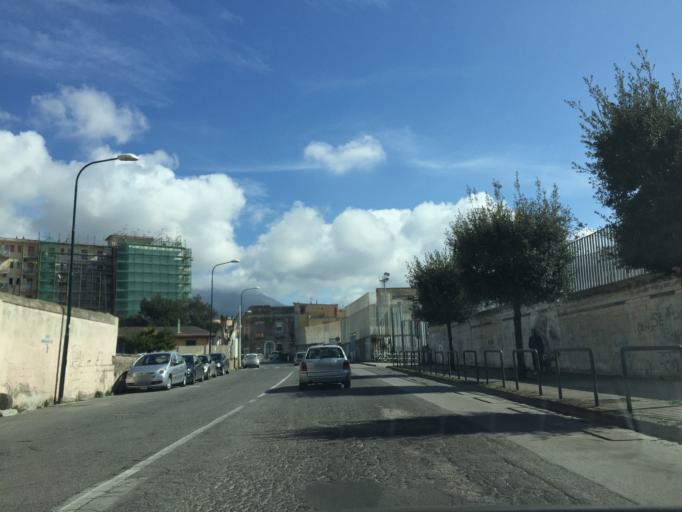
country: IT
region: Campania
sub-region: Provincia di Napoli
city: Portici
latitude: 40.8246
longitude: 14.3344
